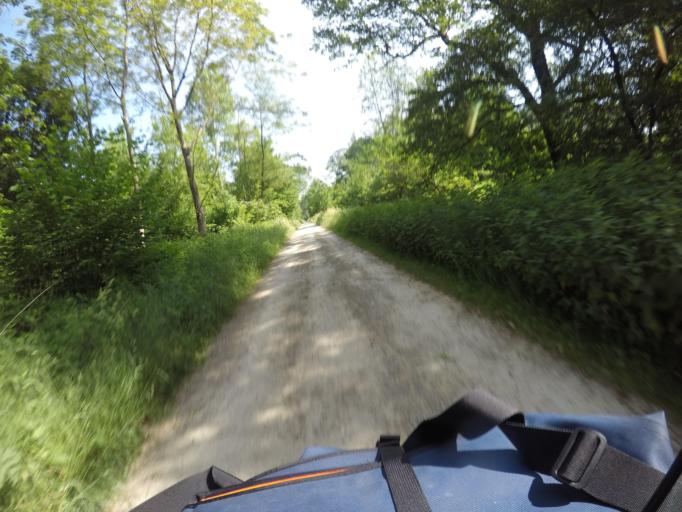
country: DE
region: Baden-Wuerttemberg
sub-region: Karlsruhe Region
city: Otigheim
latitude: 48.8988
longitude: 8.2314
